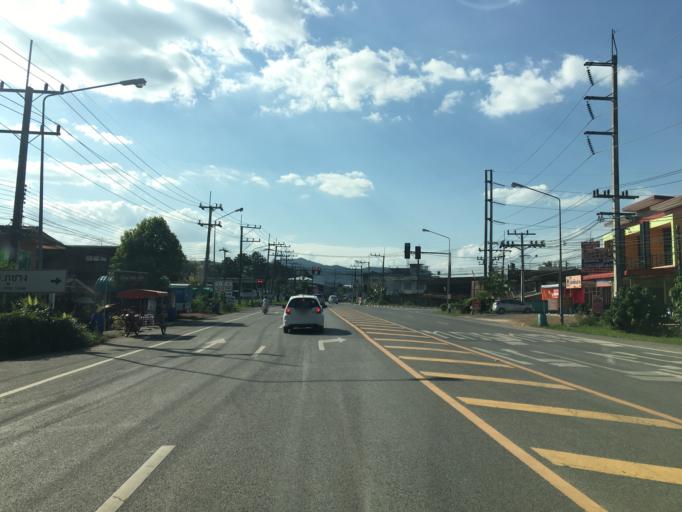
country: TH
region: Phayao
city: Chun
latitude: 19.3390
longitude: 100.1292
